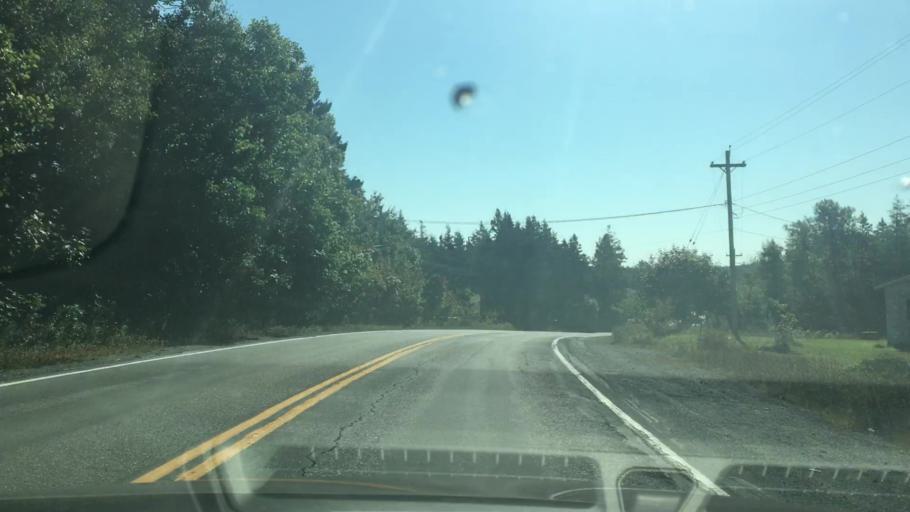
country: CA
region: Nova Scotia
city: Cole Harbour
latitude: 44.7775
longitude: -63.0582
